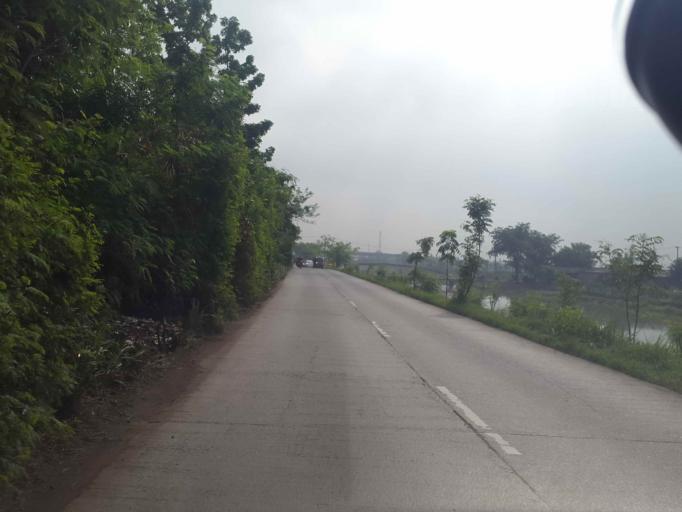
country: ID
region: West Java
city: Cikarang
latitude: -6.2952
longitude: 107.1247
